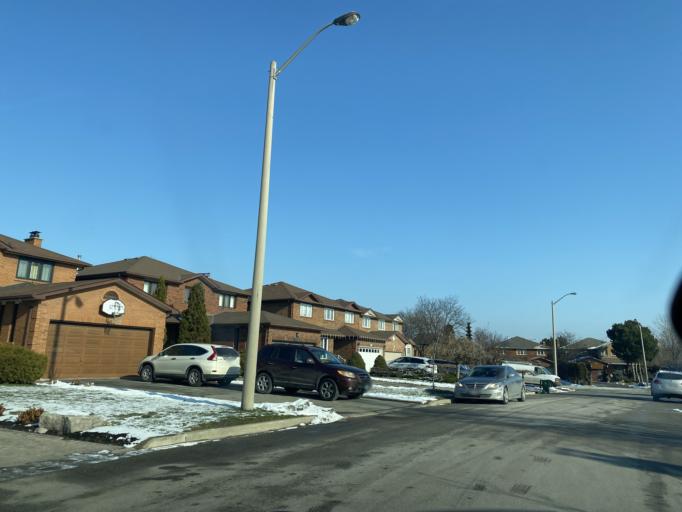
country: CA
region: Ontario
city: Etobicoke
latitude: 43.6691
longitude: -79.5720
